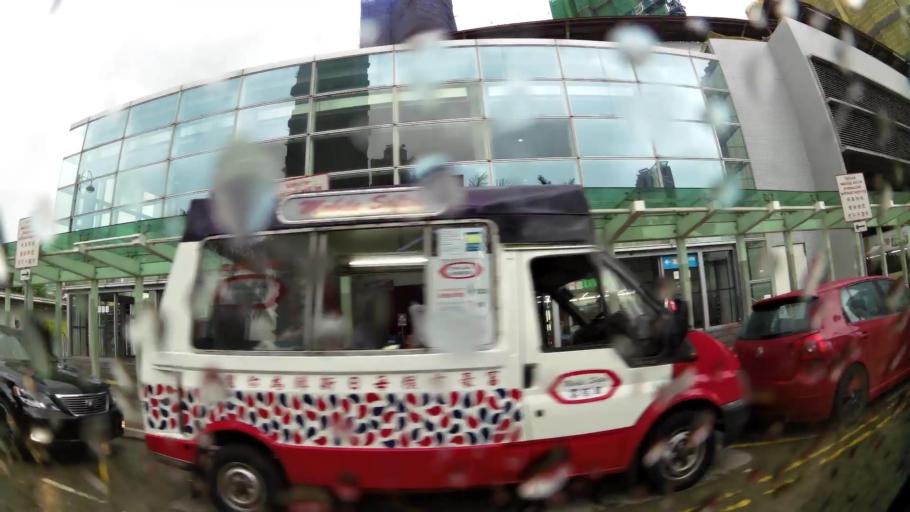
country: HK
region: Tsuen Wan
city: Tsuen Wan
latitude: 22.3672
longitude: 114.1110
